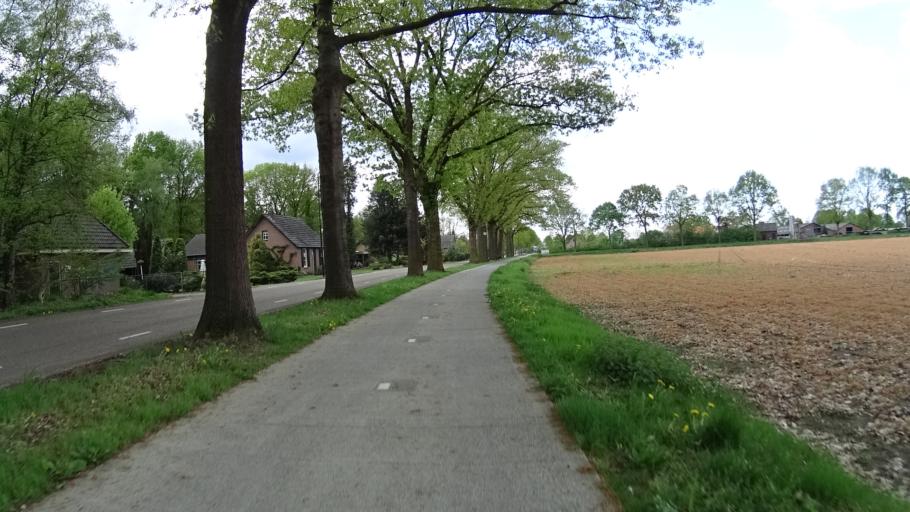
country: NL
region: North Brabant
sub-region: Gemeente Boekel
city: Boekel
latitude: 51.5929
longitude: 5.6983
